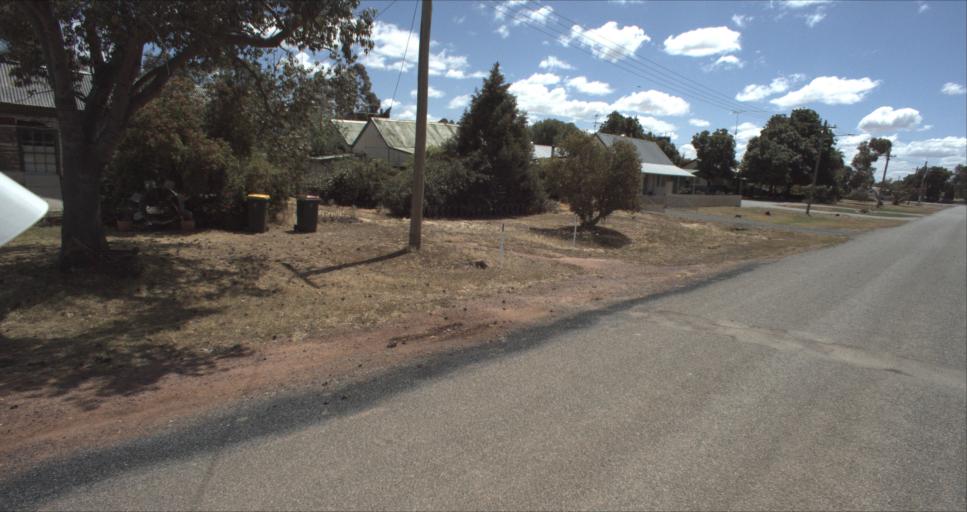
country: AU
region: New South Wales
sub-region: Murrumbidgee Shire
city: Darlington Point
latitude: -34.5195
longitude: 146.1832
